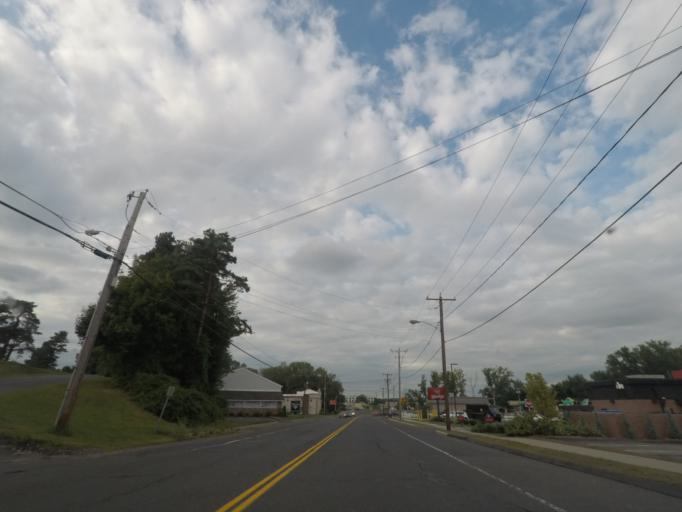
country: US
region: Massachusetts
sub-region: Hampden County
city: West Springfield
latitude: 42.1233
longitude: -72.6270
